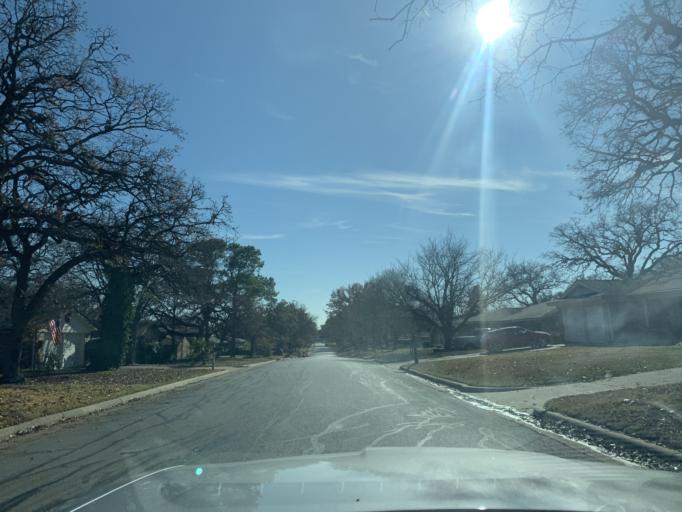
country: US
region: Texas
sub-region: Tarrant County
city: Bedford
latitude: 32.8462
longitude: -97.1510
